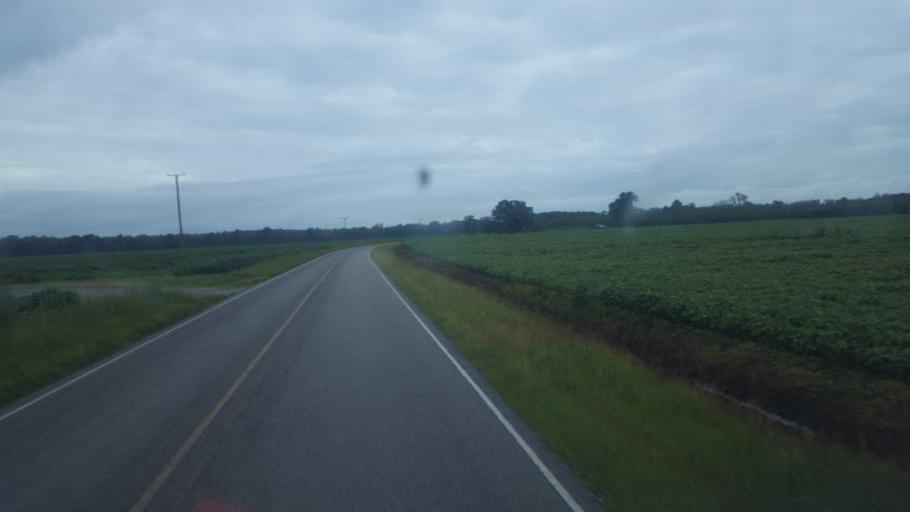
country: US
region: North Carolina
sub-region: Tyrrell County
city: Columbia
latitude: 35.9386
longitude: -76.2791
